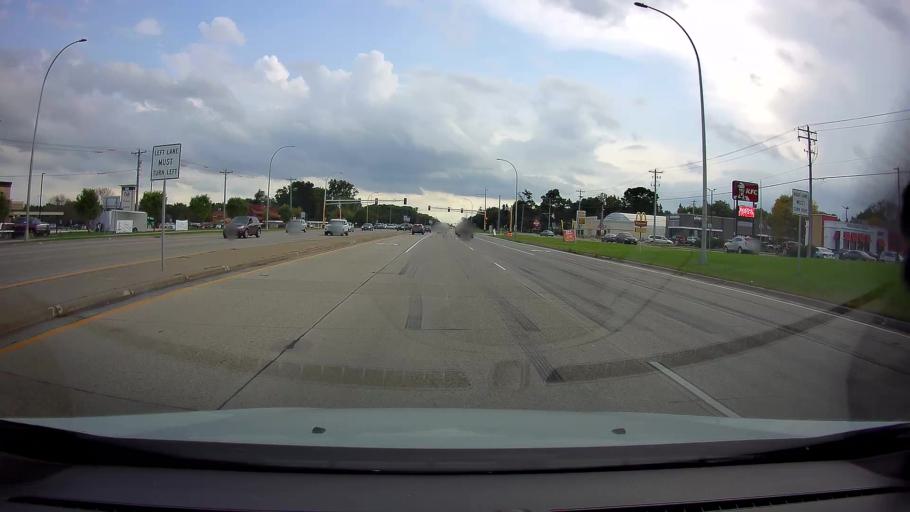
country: US
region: Minnesota
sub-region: Ramsey County
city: Roseville
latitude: 45.0045
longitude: -93.1666
